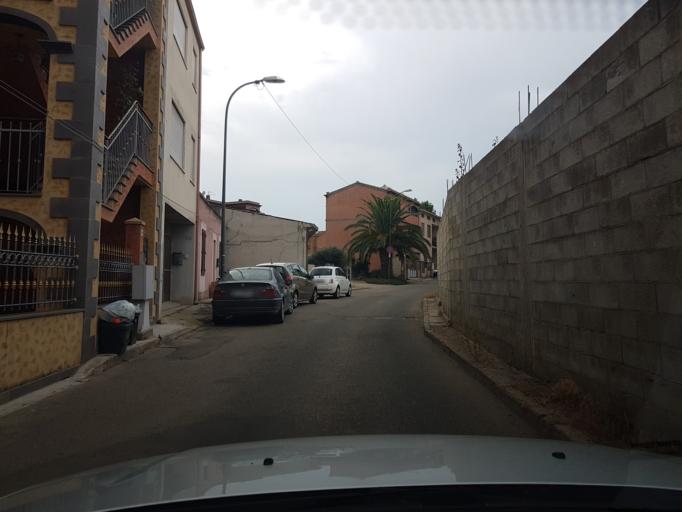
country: IT
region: Sardinia
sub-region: Provincia di Oristano
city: Donigala Fenugheddu
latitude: 39.9266
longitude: 8.5749
